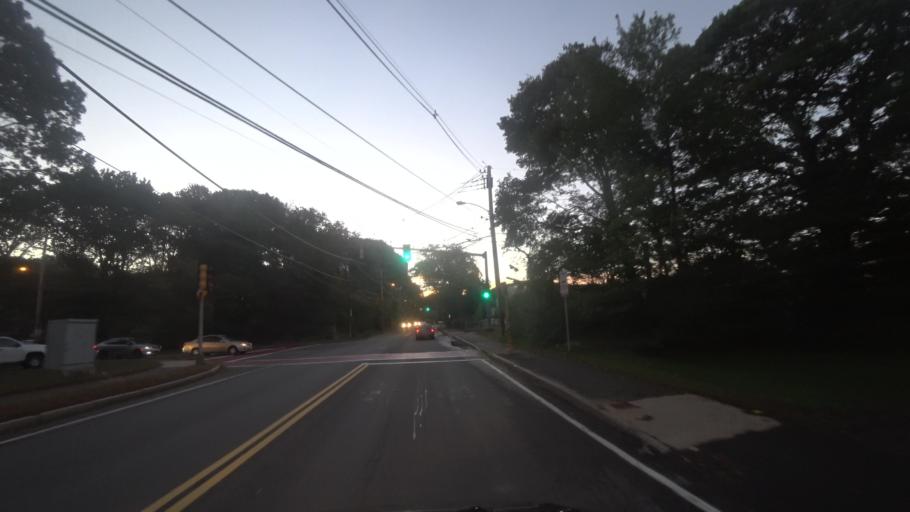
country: US
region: Massachusetts
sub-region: Essex County
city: Saugus
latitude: 42.4700
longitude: -71.0310
